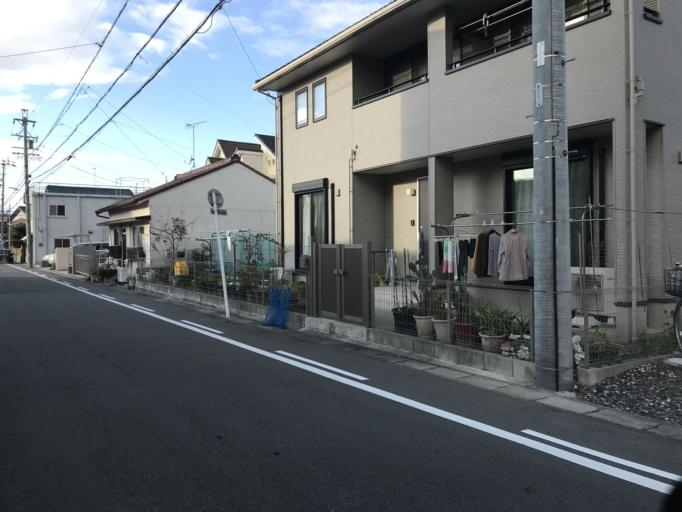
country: JP
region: Aichi
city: Nagoya-shi
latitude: 35.1981
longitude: 136.8675
